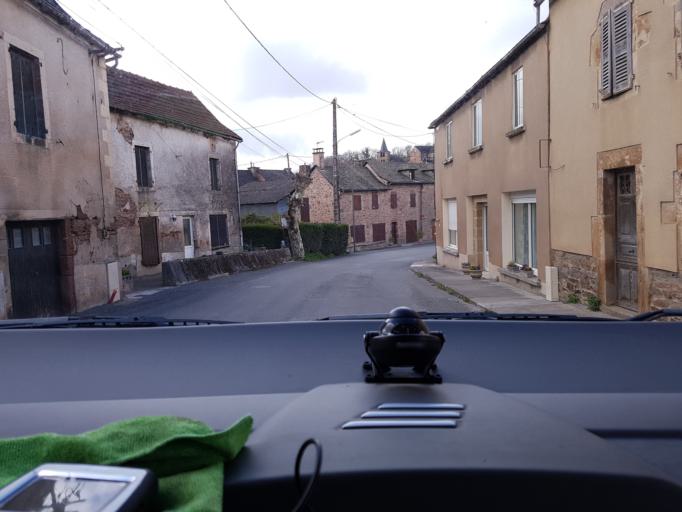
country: FR
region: Midi-Pyrenees
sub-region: Departement de l'Aveyron
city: Moyrazes
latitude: 44.3774
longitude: 2.4450
